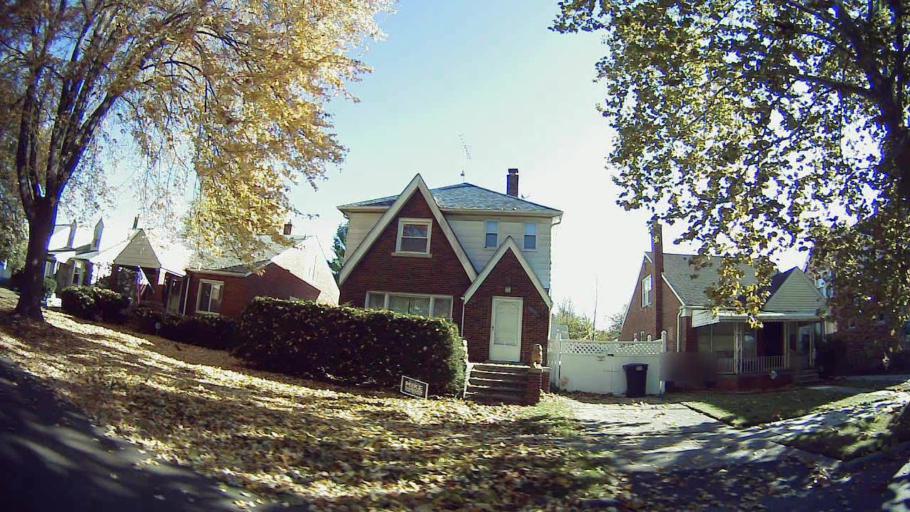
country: US
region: Michigan
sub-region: Wayne County
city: Dearborn
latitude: 42.3444
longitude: -83.2196
